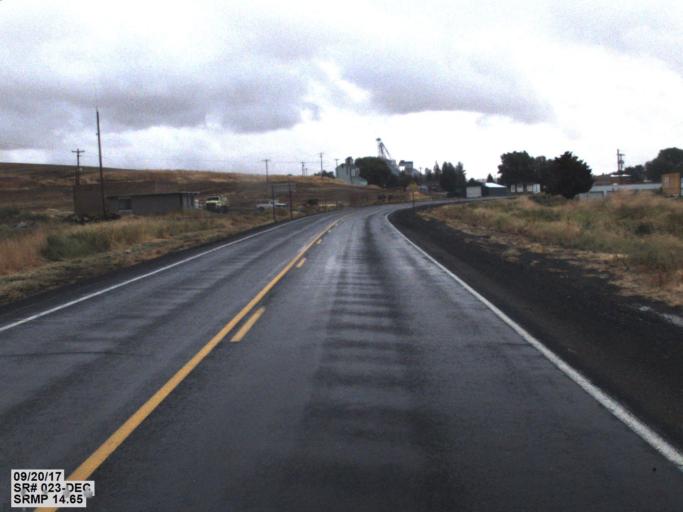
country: US
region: Washington
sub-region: Whitman County
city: Colfax
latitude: 47.0943
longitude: -117.5907
